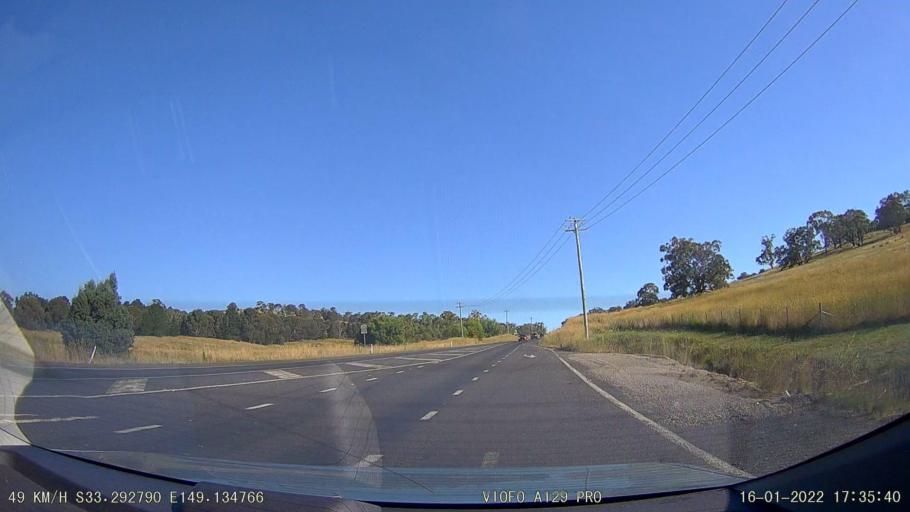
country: AU
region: New South Wales
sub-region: Orange Municipality
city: Orange
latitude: -33.2934
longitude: 149.1345
